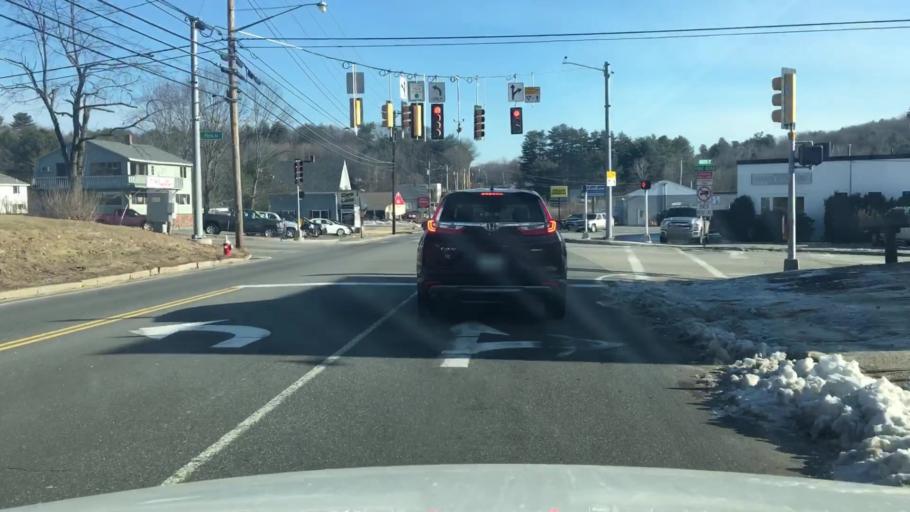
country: US
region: Maine
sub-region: Androscoggin County
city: Sabattus
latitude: 44.1006
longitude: -70.1543
